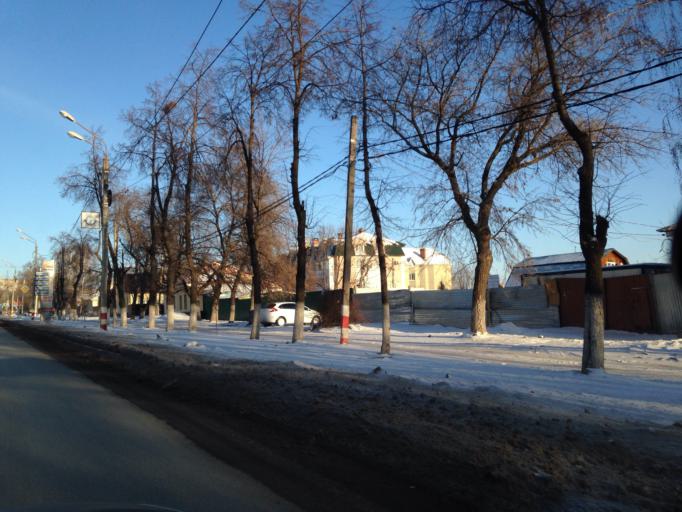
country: RU
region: Ulyanovsk
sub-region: Ulyanovskiy Rayon
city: Ulyanovsk
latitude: 54.3031
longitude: 48.3861
